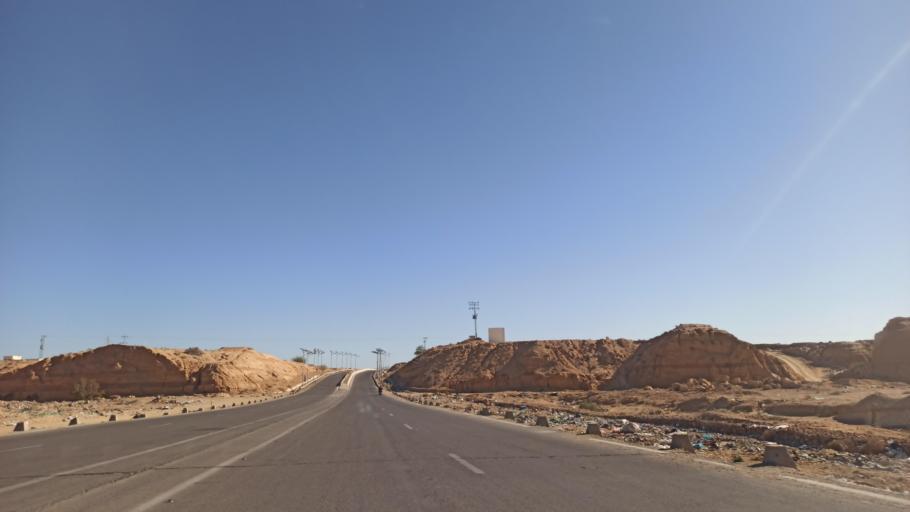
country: TN
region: Gafsa
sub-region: Gafsa Municipality
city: Gafsa
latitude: 34.4333
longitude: 8.8077
